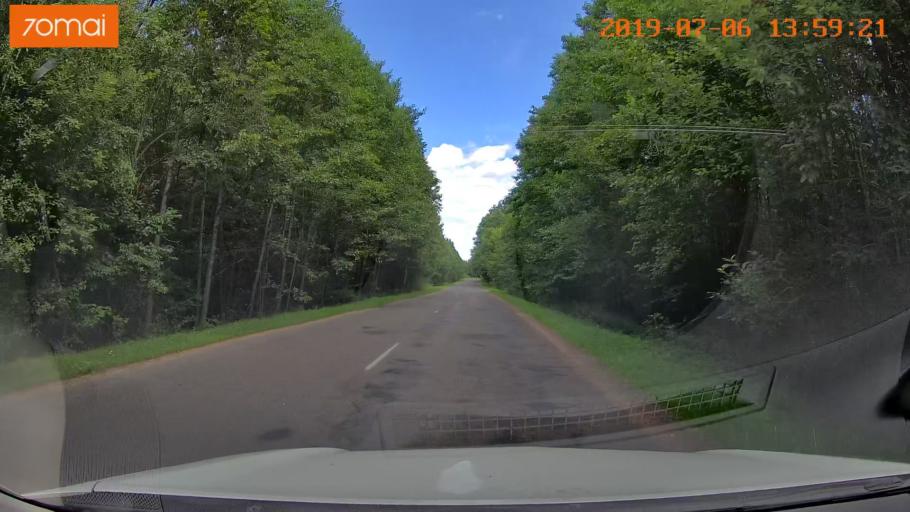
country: BY
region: Minsk
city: Ivyanyets
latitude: 53.7939
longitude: 26.8131
